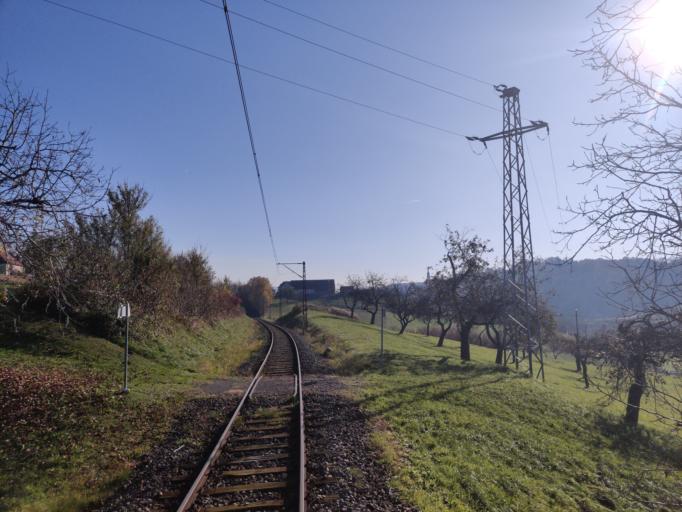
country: AT
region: Styria
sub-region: Politischer Bezirk Suedoststeiermark
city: Trautmannsdorf in Oststeiermark
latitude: 46.8819
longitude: 15.8831
